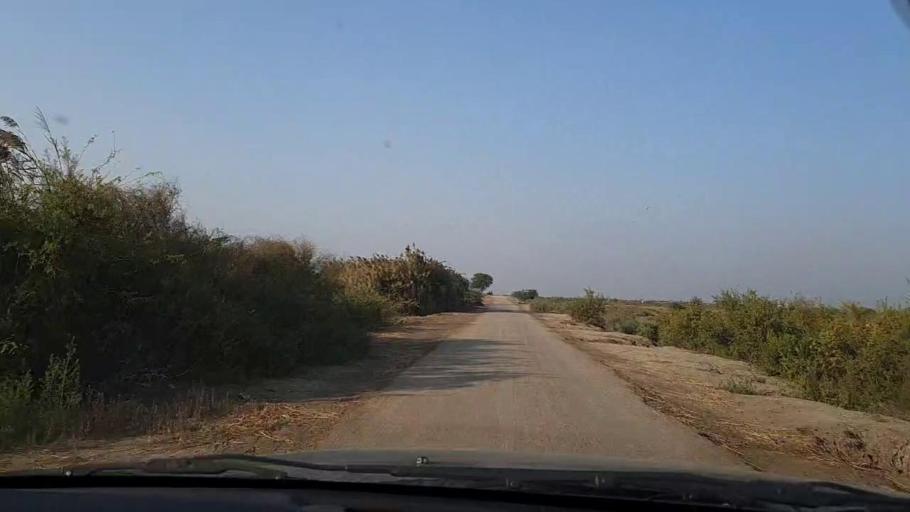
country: PK
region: Sindh
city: Chuhar Jamali
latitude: 24.3048
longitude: 67.7555
